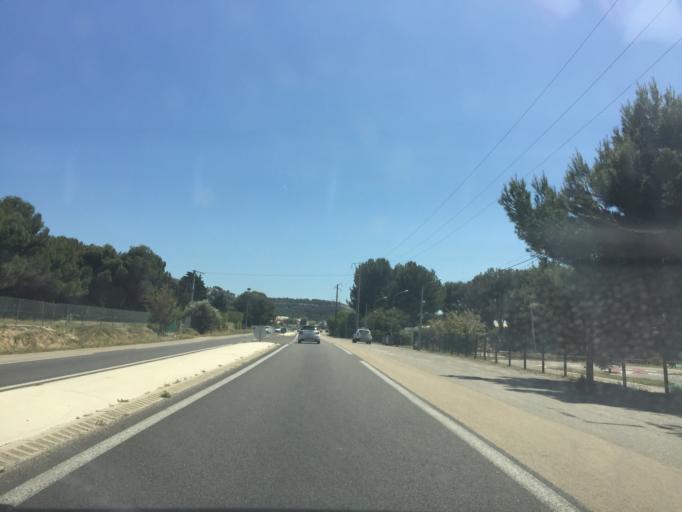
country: FR
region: Provence-Alpes-Cote d'Azur
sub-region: Departement des Bouches-du-Rhone
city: Rognac
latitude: 43.4814
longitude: 5.2253
